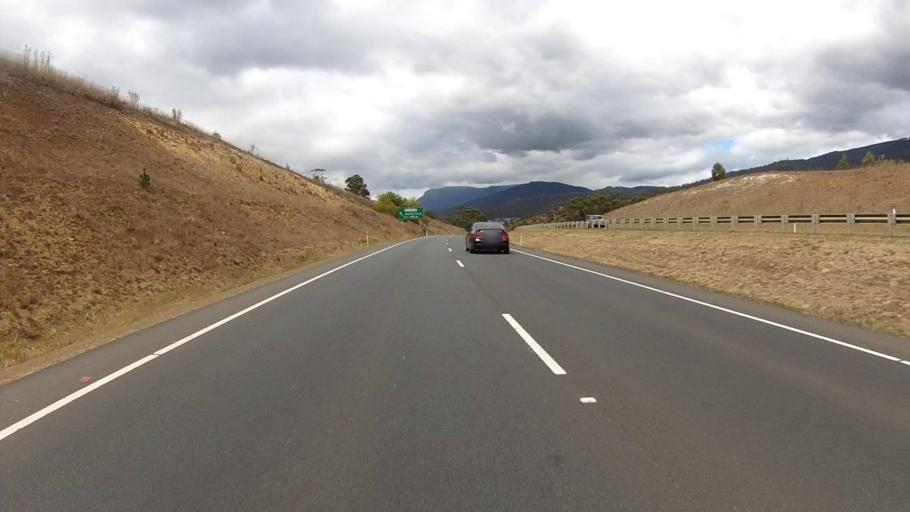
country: AU
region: Tasmania
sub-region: Glenorchy
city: Austins Ferry
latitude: -42.7738
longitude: 147.2391
